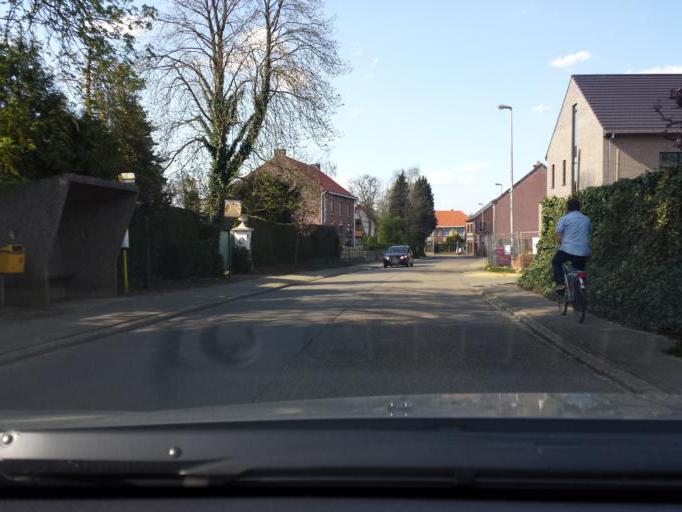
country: BE
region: Flanders
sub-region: Provincie Limburg
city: Halen
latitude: 50.9779
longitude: 5.1059
